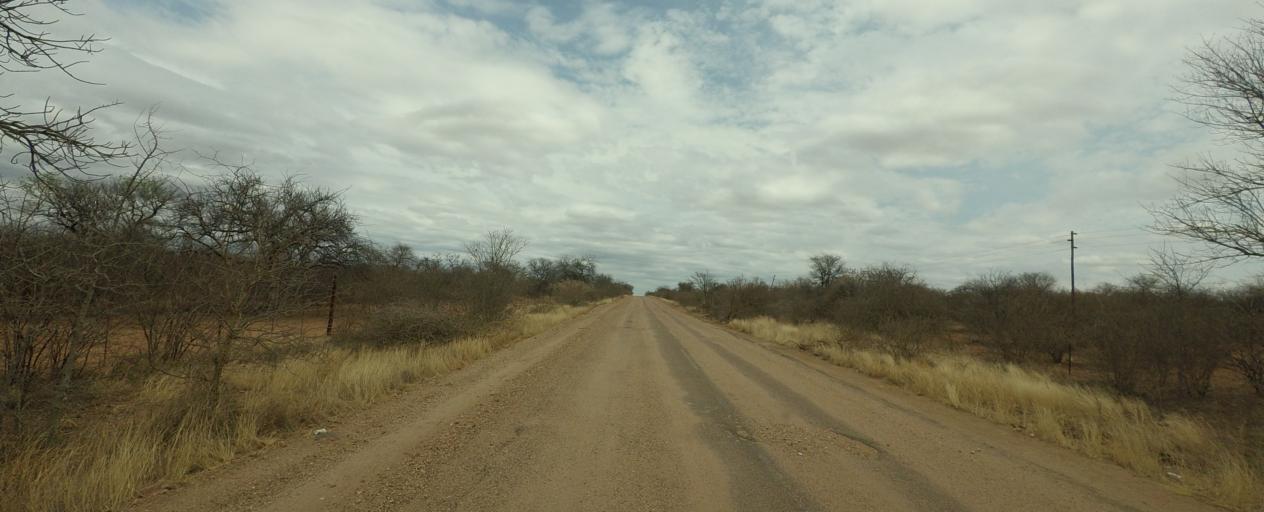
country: BW
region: Central
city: Mathathane
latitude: -22.6707
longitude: 28.6835
